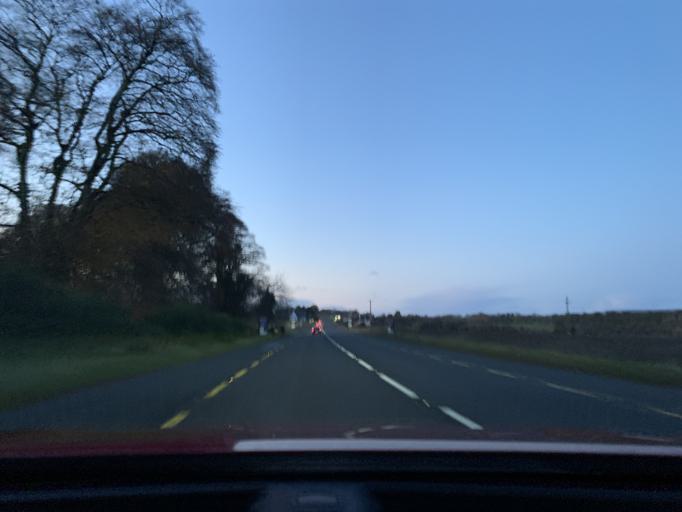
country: IE
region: Connaught
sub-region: County Leitrim
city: Carrick-on-Shannon
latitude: 53.9628
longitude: -8.1940
